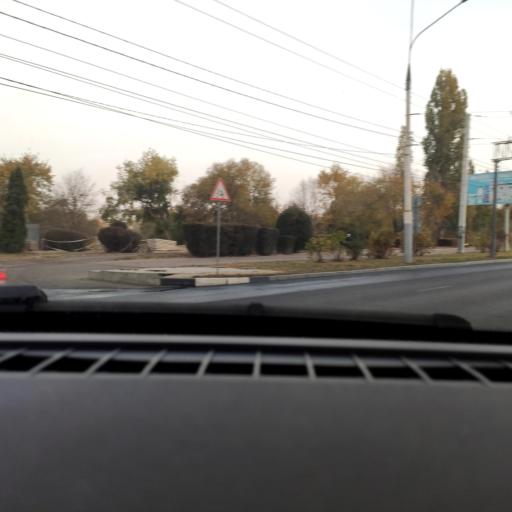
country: RU
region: Voronezj
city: Voronezh
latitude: 51.6582
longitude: 39.2453
